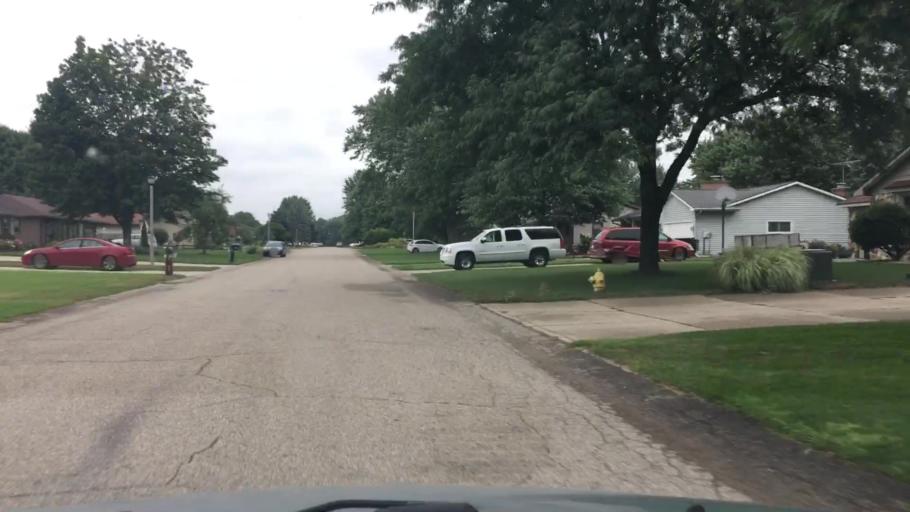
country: US
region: Michigan
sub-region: Ottawa County
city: Hudsonville
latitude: 42.9023
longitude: -85.8452
